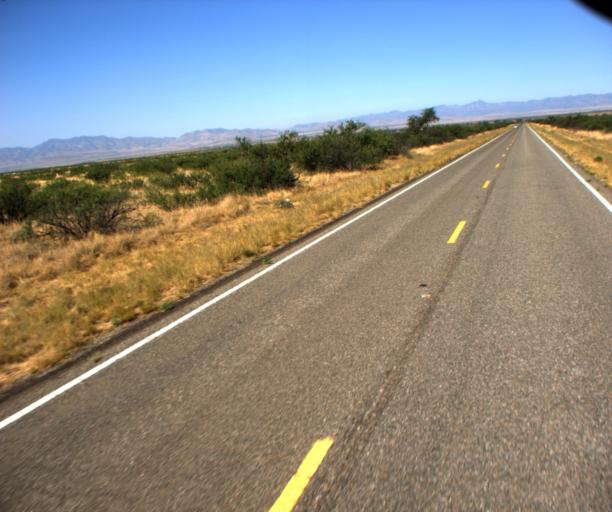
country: US
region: Arizona
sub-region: Graham County
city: Swift Trail Junction
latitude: 32.5850
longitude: -109.9326
